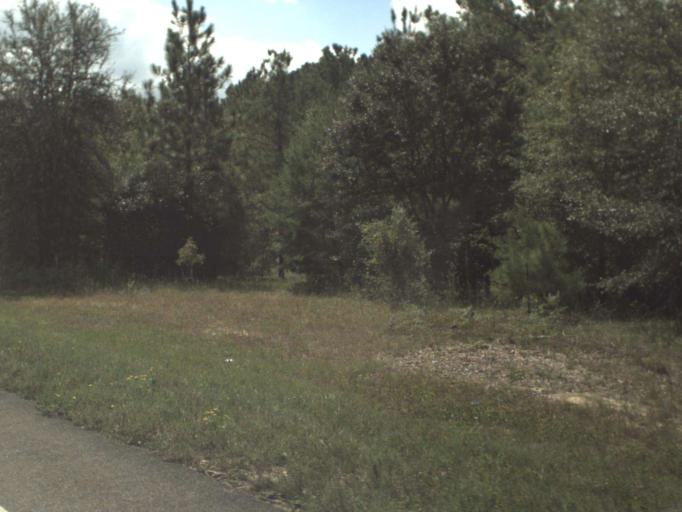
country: US
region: Florida
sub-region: Walton County
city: Freeport
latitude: 30.5576
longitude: -85.9178
